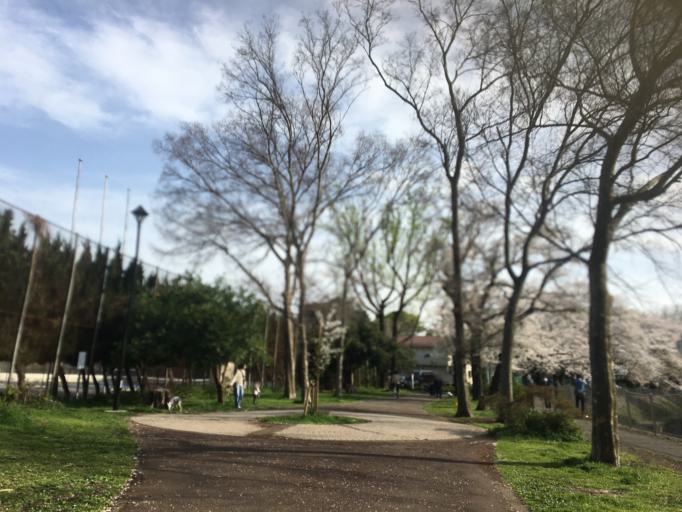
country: JP
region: Tokyo
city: Tokyo
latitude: 35.6940
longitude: 139.6341
